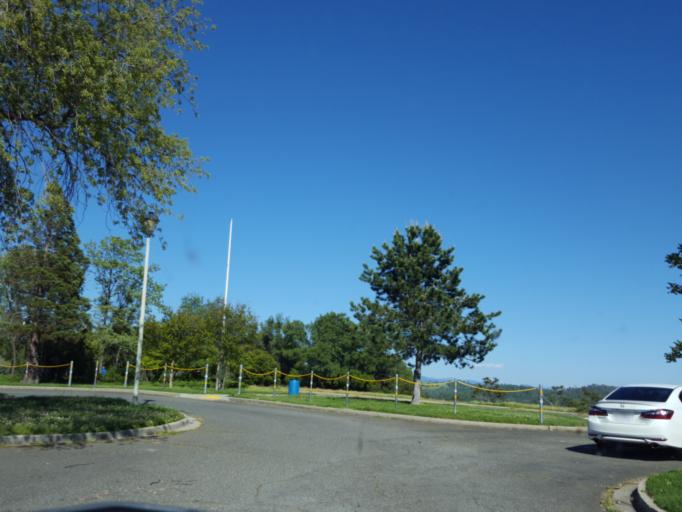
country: US
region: California
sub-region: Placer County
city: Auburn
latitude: 38.8888
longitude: -121.0685
